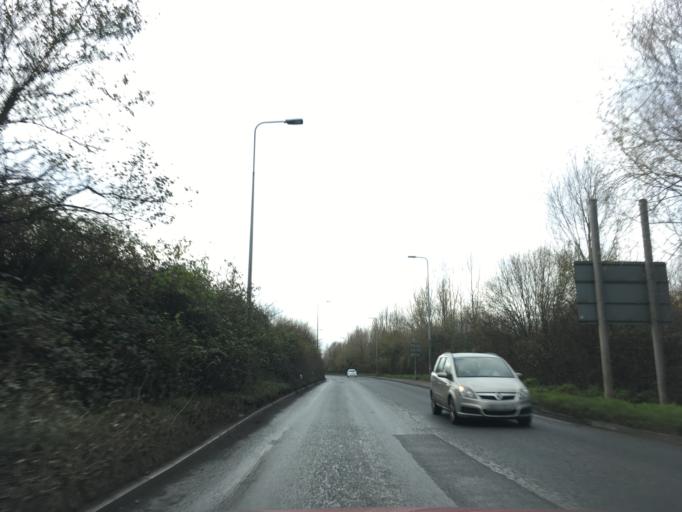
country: GB
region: Wales
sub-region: Cardiff
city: Cardiff
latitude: 51.4979
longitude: -3.1261
